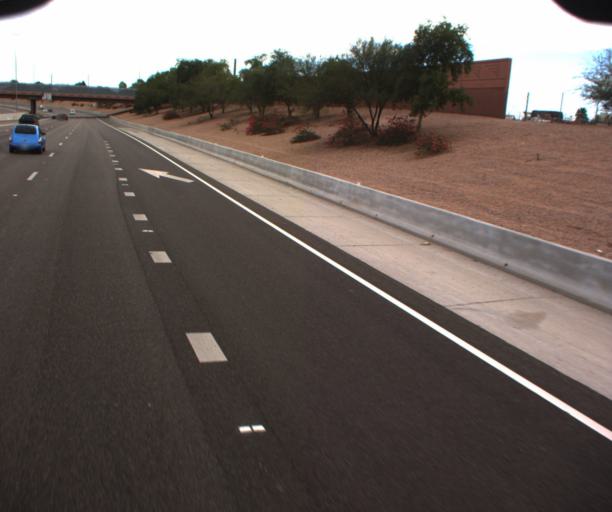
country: US
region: Arizona
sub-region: Maricopa County
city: Mesa
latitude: 33.4580
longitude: -111.8335
